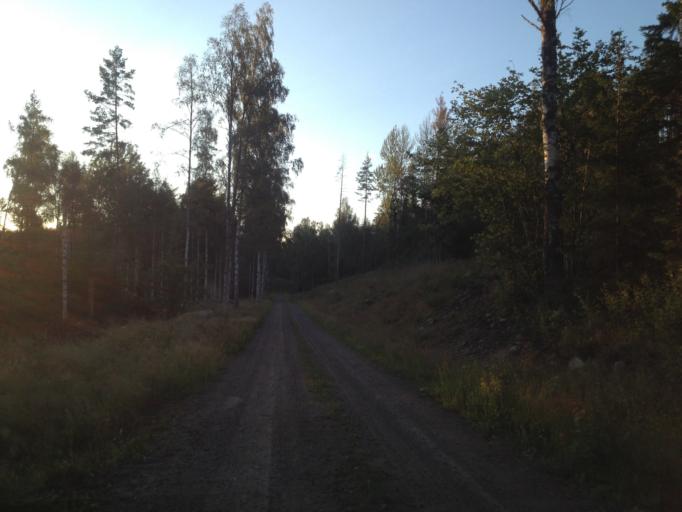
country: SE
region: Kalmar
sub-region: Vasterviks Kommun
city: Overum
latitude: 58.0126
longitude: 16.1202
